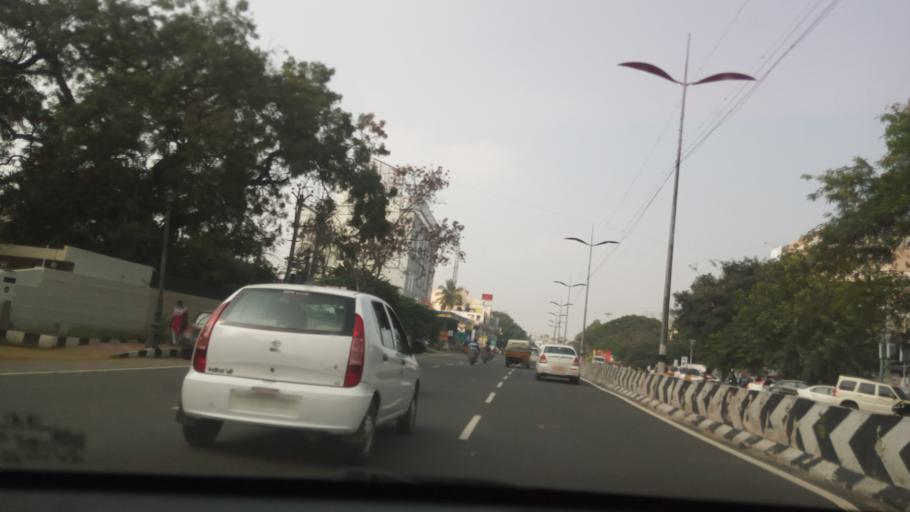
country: IN
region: Tamil Nadu
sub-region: Coimbatore
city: Coimbatore
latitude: 11.0065
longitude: 76.9766
